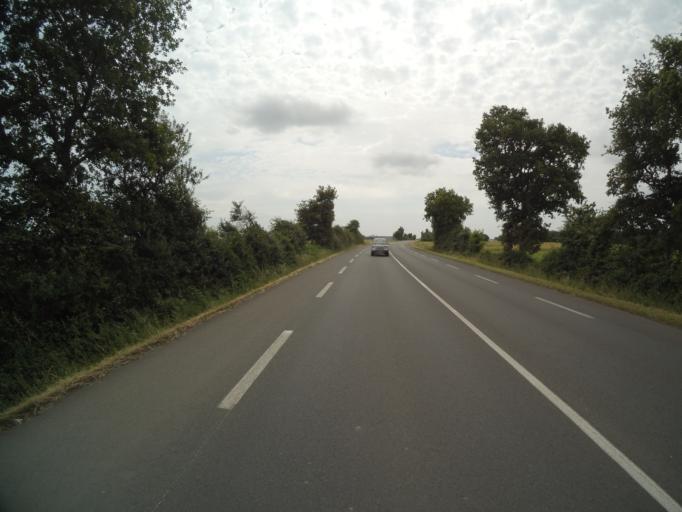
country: FR
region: Pays de la Loire
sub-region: Departement de la Vendee
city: Chavagnes-en-Paillers
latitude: 46.9203
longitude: -1.2471
